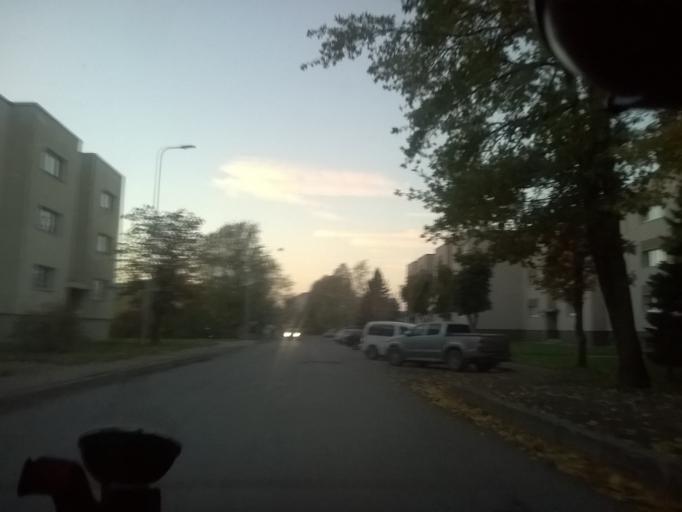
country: EE
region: Laeaene
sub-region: Haapsalu linn
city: Haapsalu
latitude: 58.9406
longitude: 23.5514
